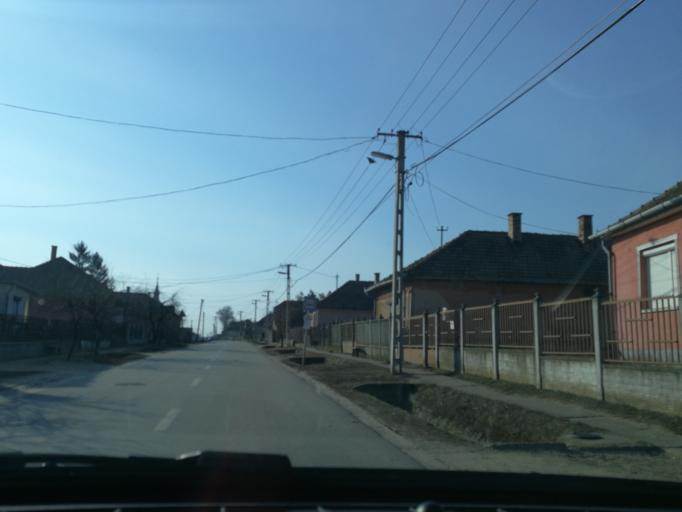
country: HU
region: Szabolcs-Szatmar-Bereg
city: Apagy
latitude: 48.0245
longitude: 21.9602
